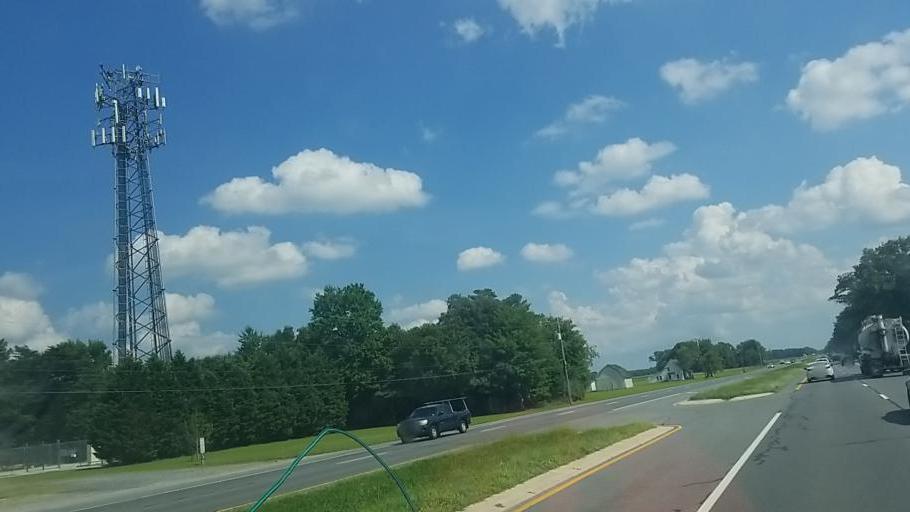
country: US
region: Delaware
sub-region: Sussex County
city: Millsboro
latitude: 38.6305
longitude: -75.3469
